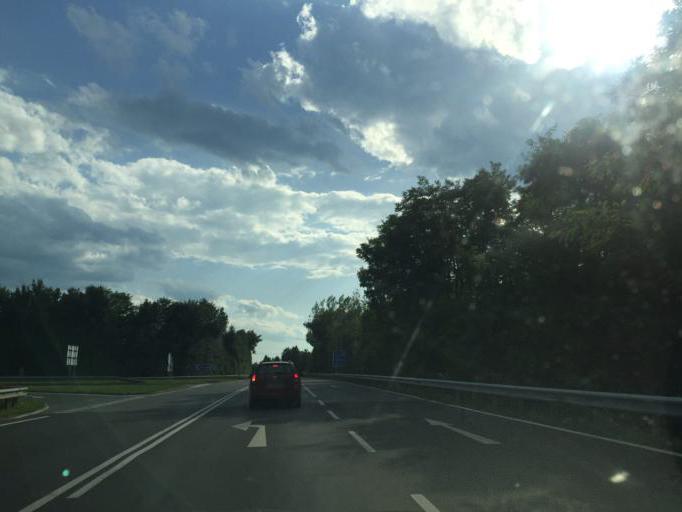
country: AT
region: Styria
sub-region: Politischer Bezirk Leibnitz
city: Sankt Veit am Vogau
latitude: 46.7452
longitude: 15.6128
